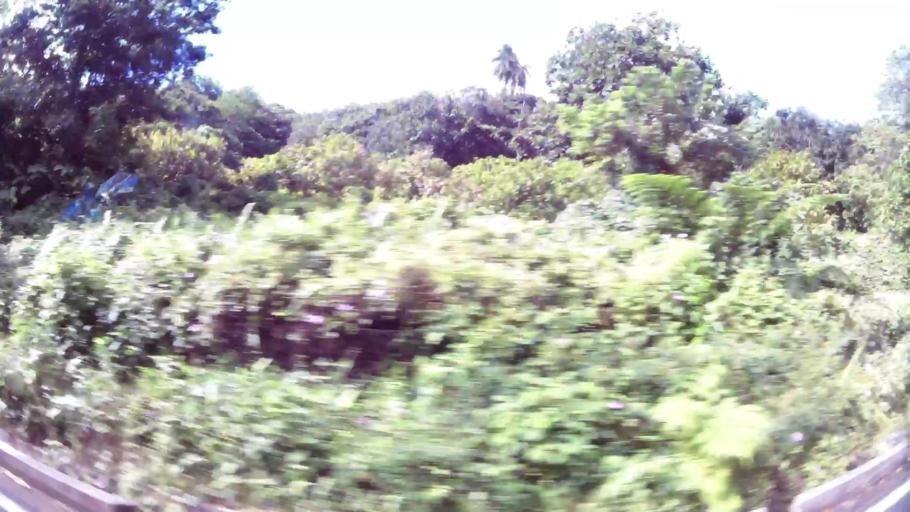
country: DM
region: Saint Andrew
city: Marigot
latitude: 15.5139
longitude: -61.2779
